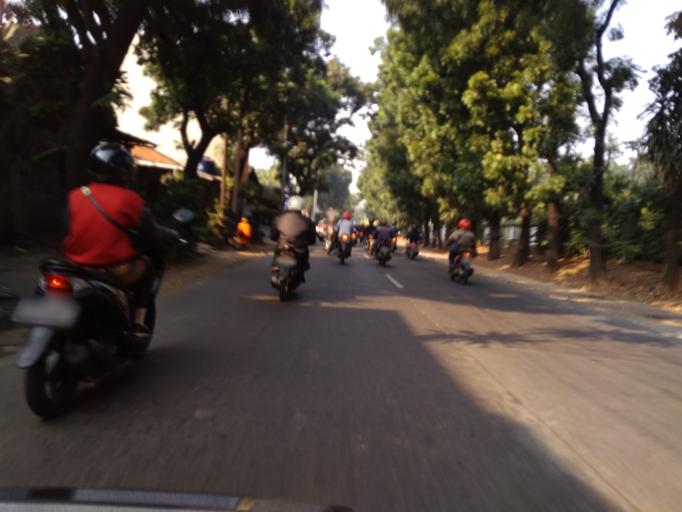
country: ID
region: Jakarta Raya
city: Jakarta
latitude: -6.2998
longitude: 106.8404
